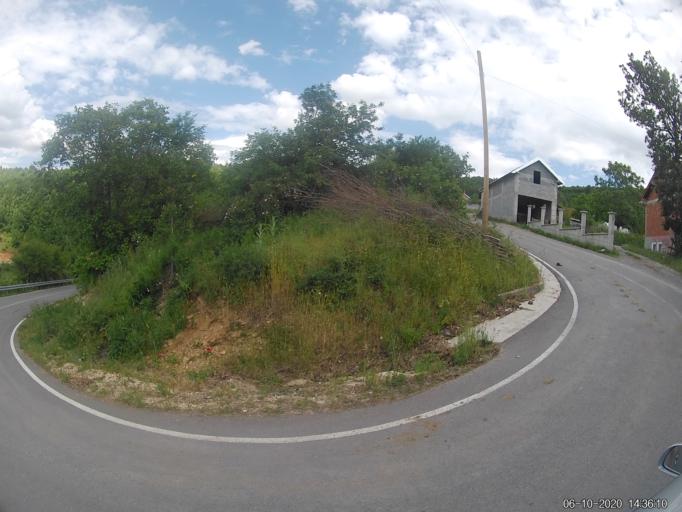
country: XK
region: Prizren
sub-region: Komuna e Therandes
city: Budakovo
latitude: 42.4113
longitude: 20.9365
